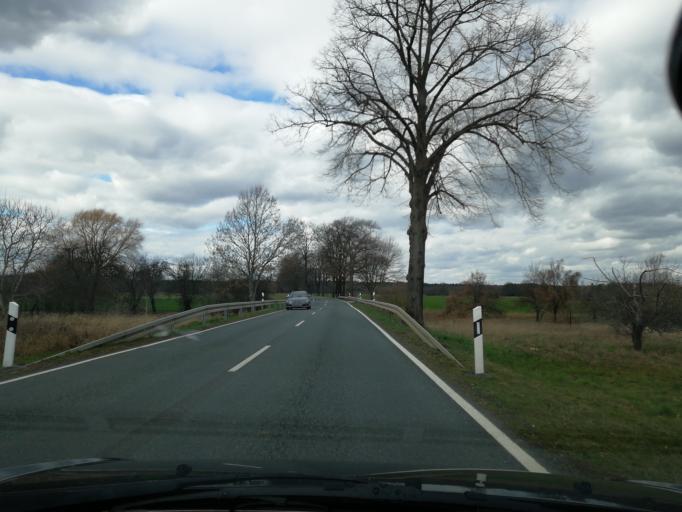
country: DE
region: Brandenburg
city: Altdobern
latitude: 51.6910
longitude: 14.0981
